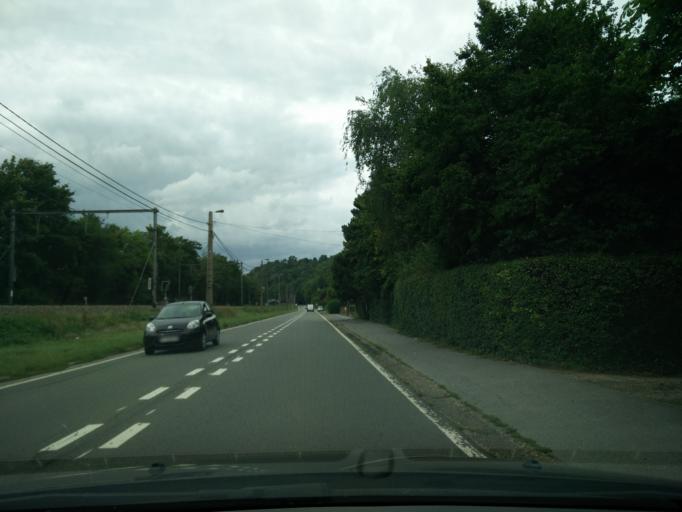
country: BE
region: Wallonia
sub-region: Province de Liege
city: Vise
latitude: 50.7145
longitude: 5.6877
